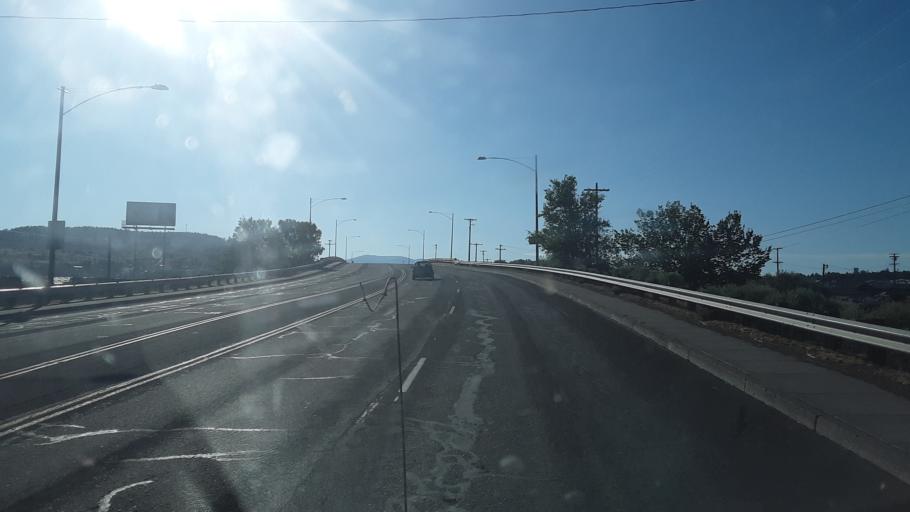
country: US
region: Oregon
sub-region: Klamath County
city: Klamath Falls
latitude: 42.2172
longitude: -121.7687
